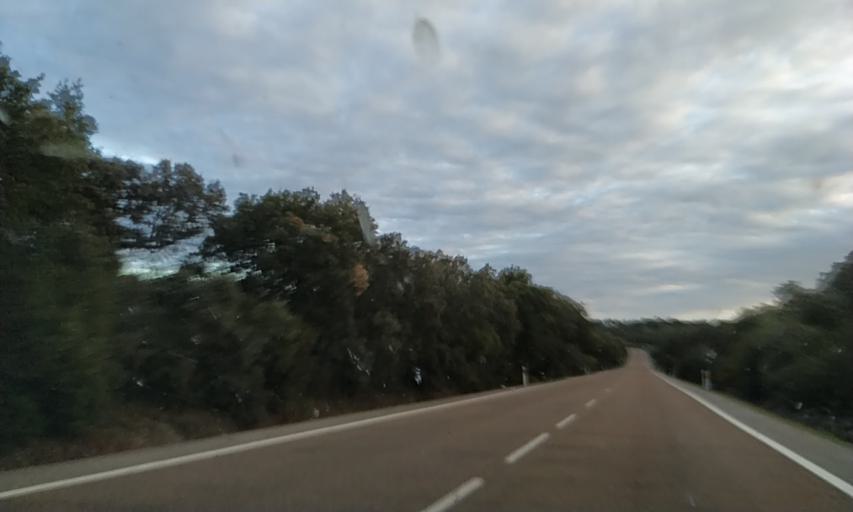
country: ES
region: Extremadura
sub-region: Provincia de Badajoz
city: Puebla de Obando
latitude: 39.2516
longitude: -6.5563
